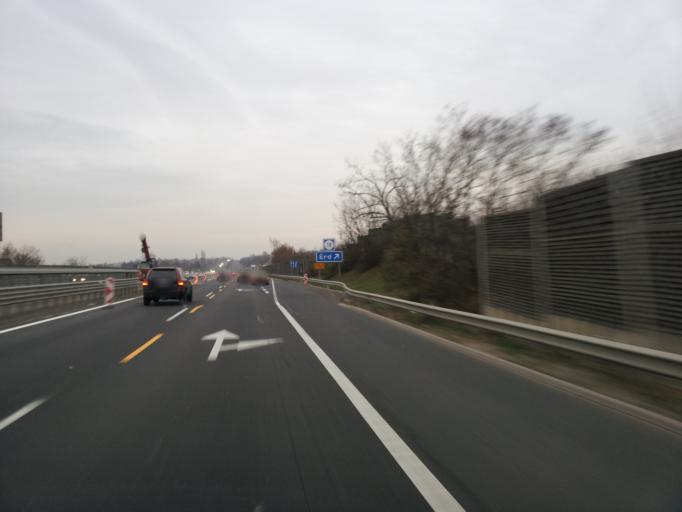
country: HU
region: Pest
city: Toeroekbalint
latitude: 47.4184
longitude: 18.8828
